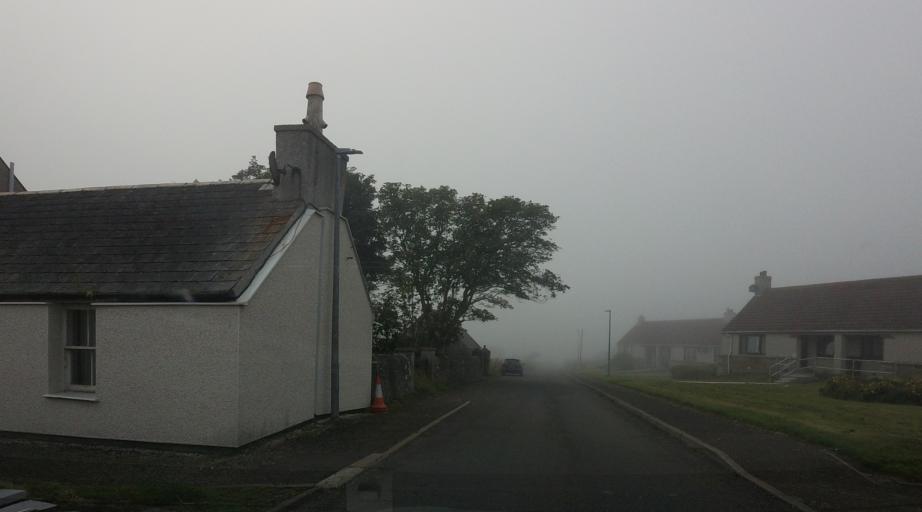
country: GB
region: Scotland
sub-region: Highland
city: Wick
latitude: 58.2994
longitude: -3.2843
